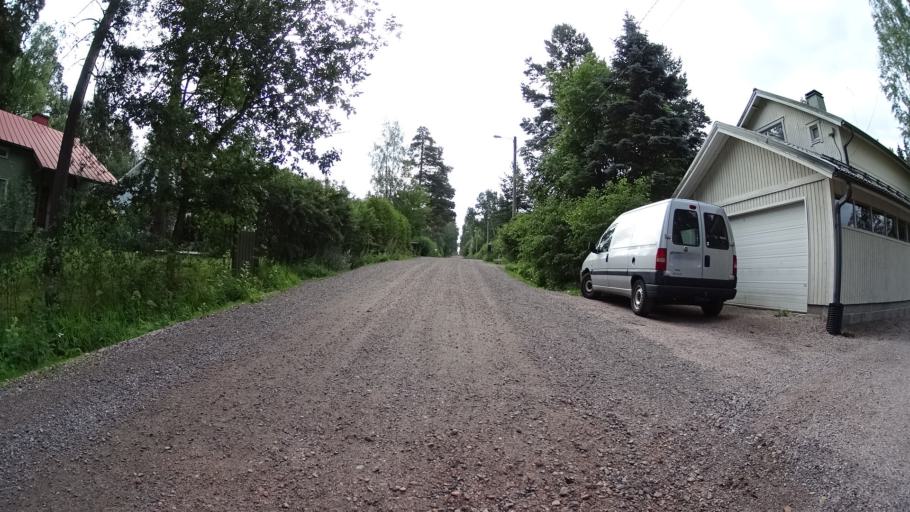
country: FI
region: Uusimaa
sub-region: Helsinki
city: Kilo
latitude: 60.2396
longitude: 24.8010
